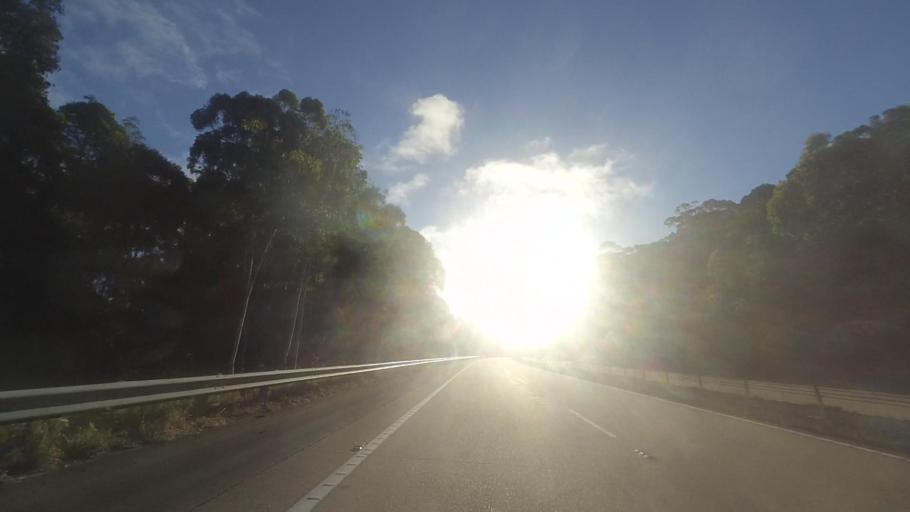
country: AU
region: New South Wales
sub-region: Great Lakes
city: Bulahdelah
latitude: -32.3868
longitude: 152.2581
